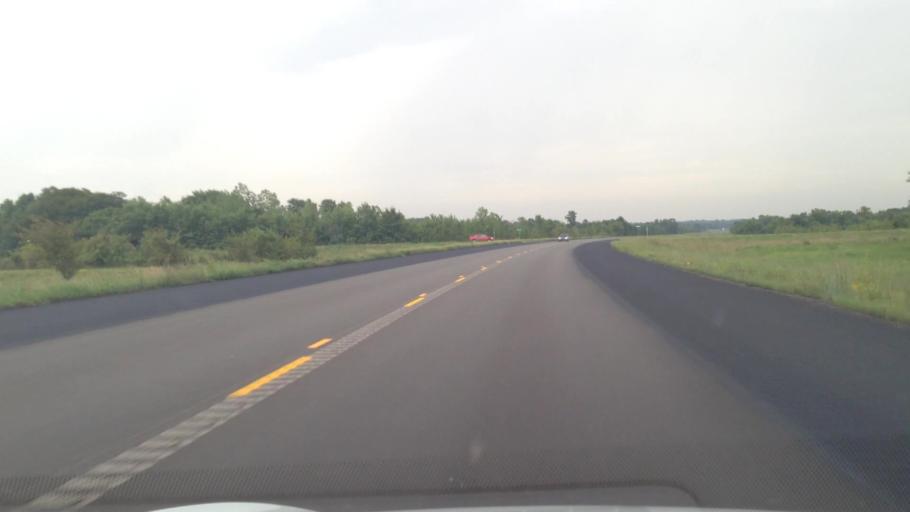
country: US
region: Kansas
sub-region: Cherokee County
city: Baxter Springs
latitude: 37.0465
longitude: -94.7135
